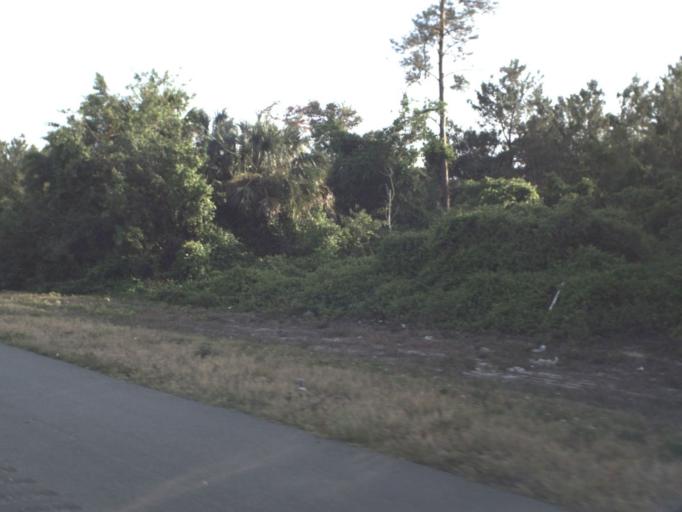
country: US
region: Florida
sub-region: Brevard County
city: Mims
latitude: 28.6322
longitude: -80.8560
